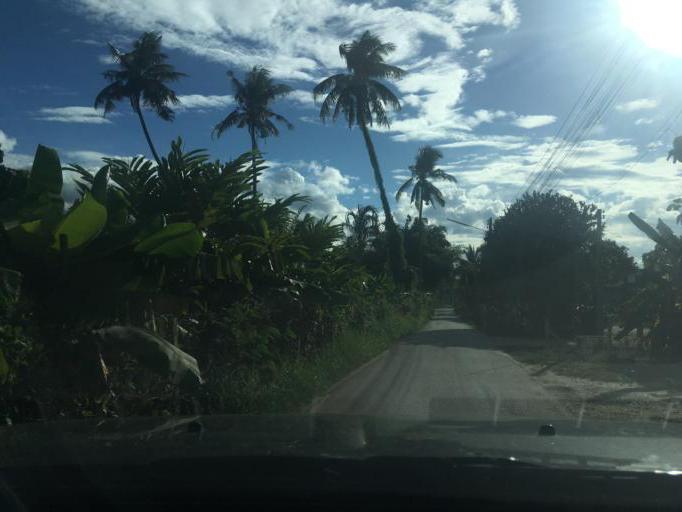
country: TH
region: Chiang Mai
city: San Sai
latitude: 18.9638
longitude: 98.9808
